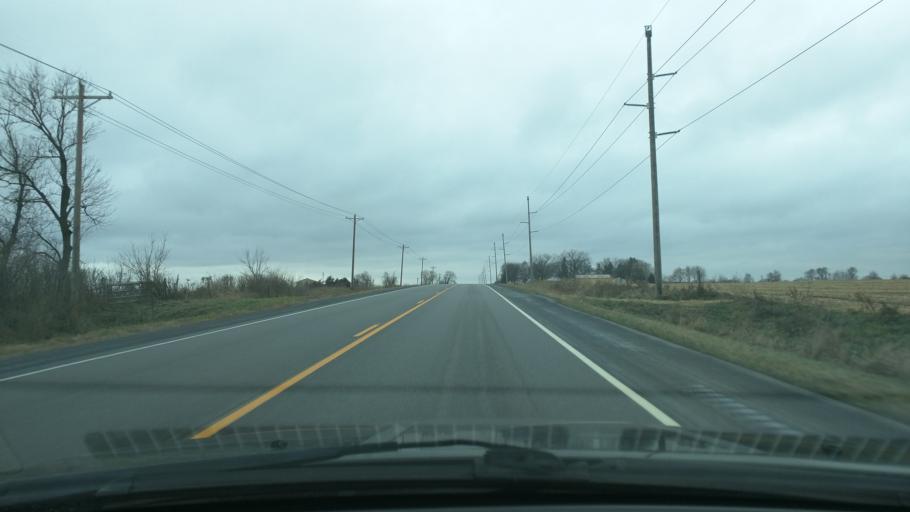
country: US
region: Minnesota
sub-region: Dakota County
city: Hastings
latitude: 44.7384
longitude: -92.9232
